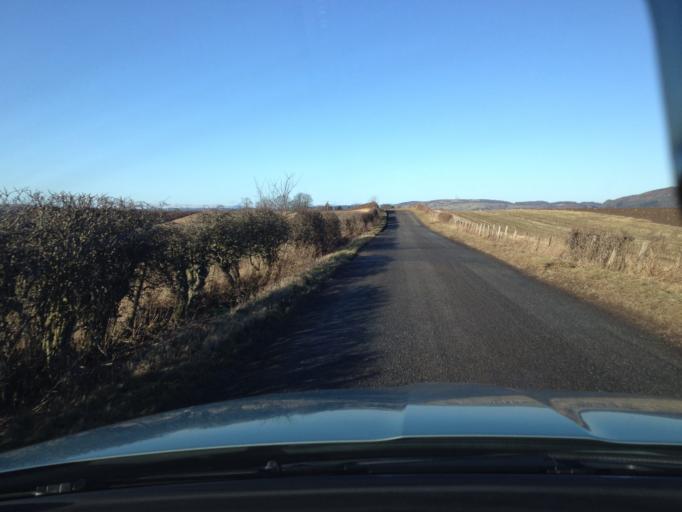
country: GB
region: Scotland
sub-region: Perth and Kinross
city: Bridge of Earn
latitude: 56.3302
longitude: -3.3829
